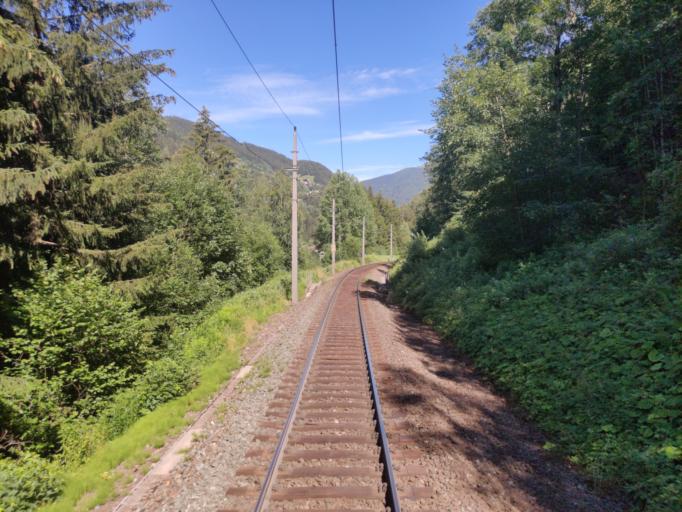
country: AT
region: Tyrol
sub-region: Politischer Bezirk Landeck
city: Strengen
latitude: 47.1278
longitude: 10.4459
